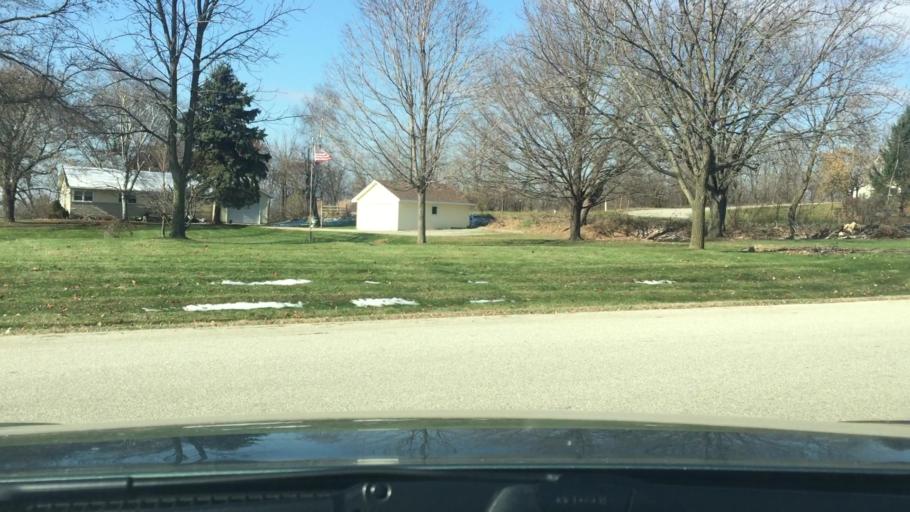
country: US
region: Wisconsin
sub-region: Jefferson County
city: Jefferson
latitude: 43.0372
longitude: -88.8068
